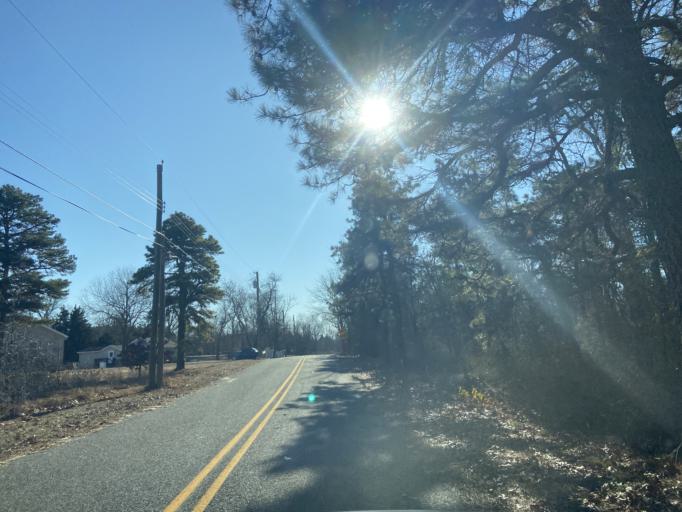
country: US
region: New Jersey
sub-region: Cumberland County
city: Vineland
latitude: 39.4939
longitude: -75.0724
